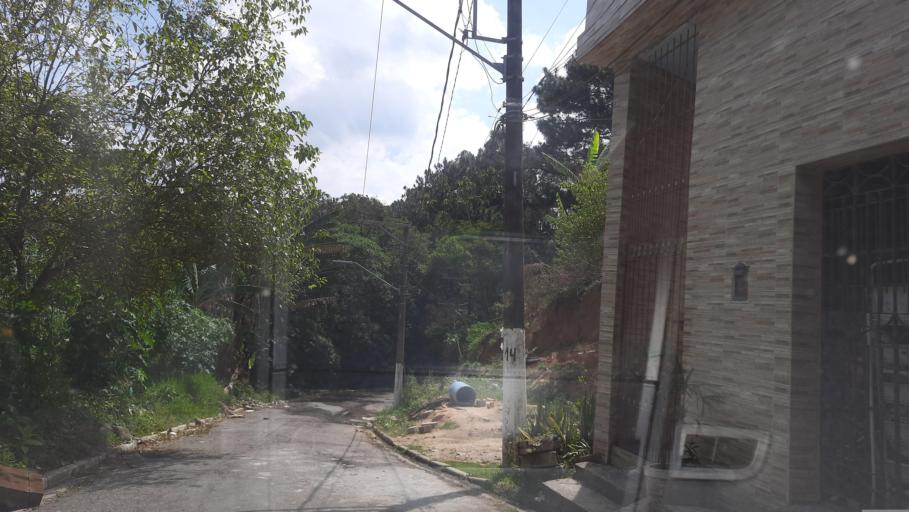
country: BR
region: Sao Paulo
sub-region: Caieiras
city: Caieiras
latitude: -23.4178
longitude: -46.7218
